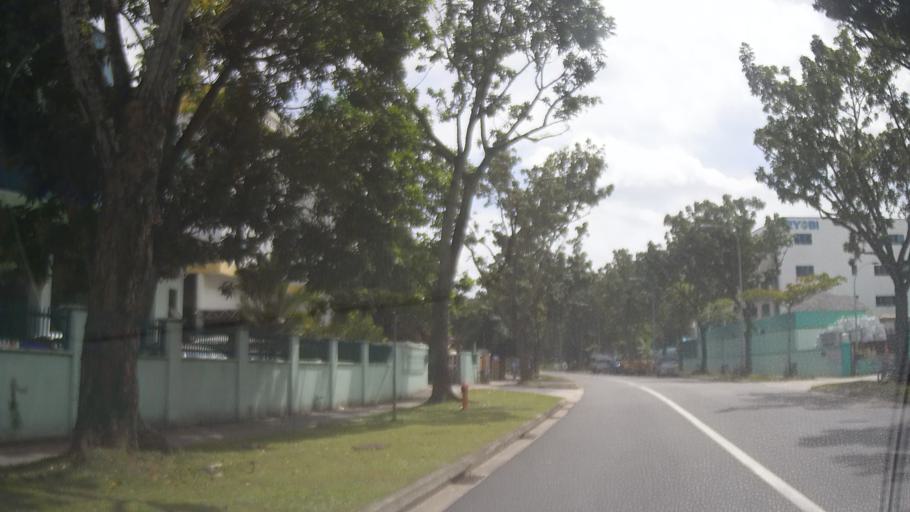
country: MY
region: Johor
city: Johor Bahru
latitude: 1.4108
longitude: 103.7435
